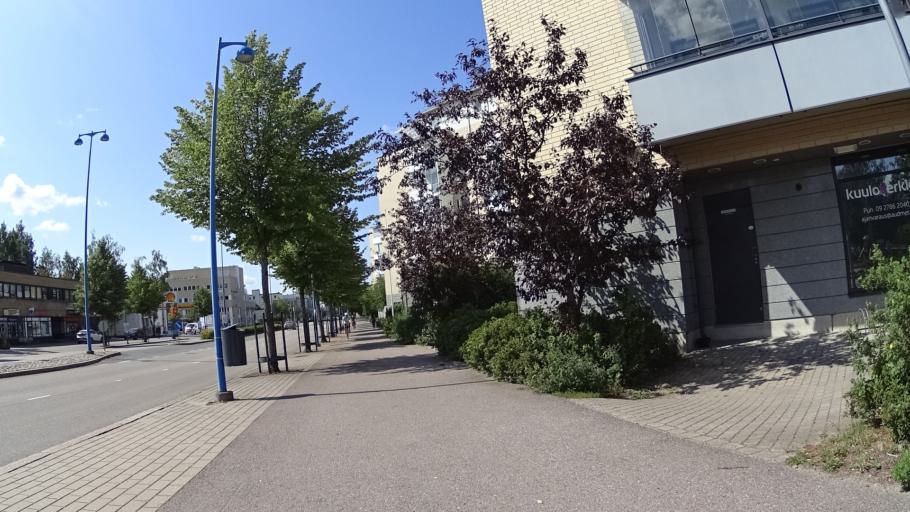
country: FI
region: Uusimaa
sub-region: Helsinki
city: Jaervenpaeae
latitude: 60.4748
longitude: 25.0866
